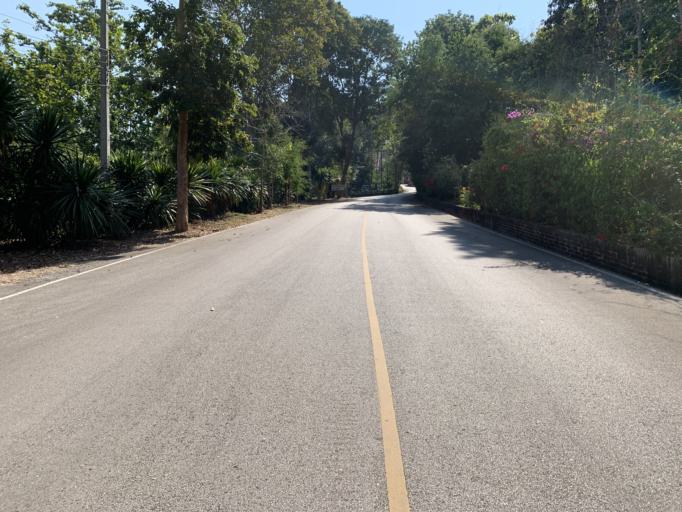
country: TH
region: Loei
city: Dan Sai
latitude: 17.2673
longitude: 101.1419
